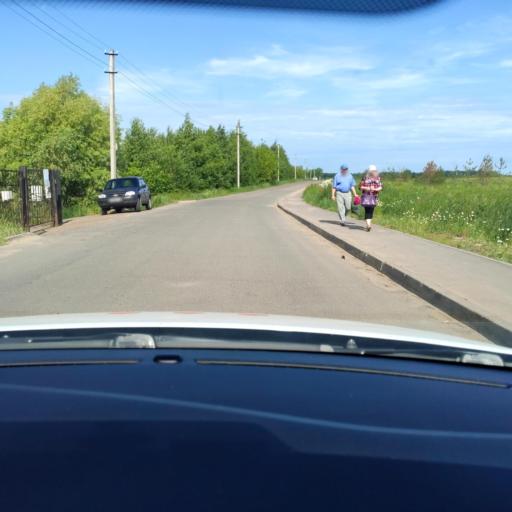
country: RU
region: Tatarstan
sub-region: Gorod Kazan'
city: Kazan
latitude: 55.8904
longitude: 49.0942
